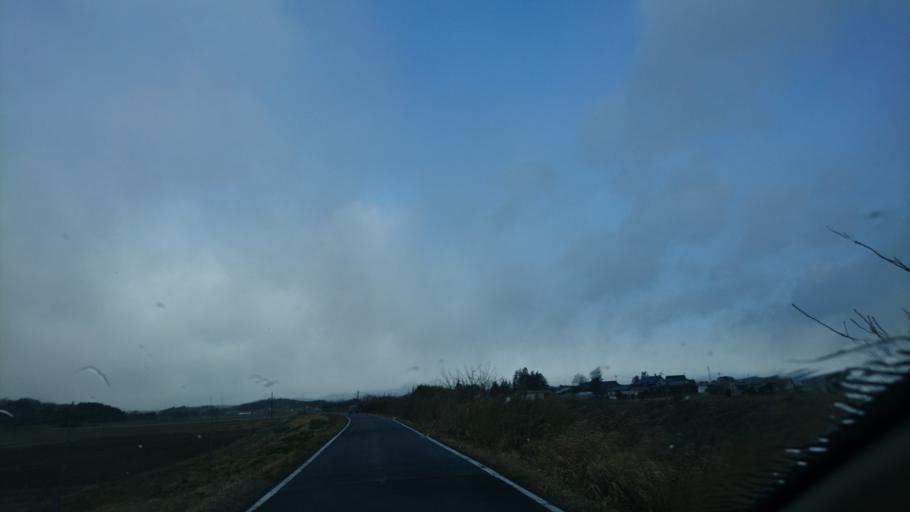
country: JP
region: Iwate
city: Ichinoseki
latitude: 38.7714
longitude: 141.0323
